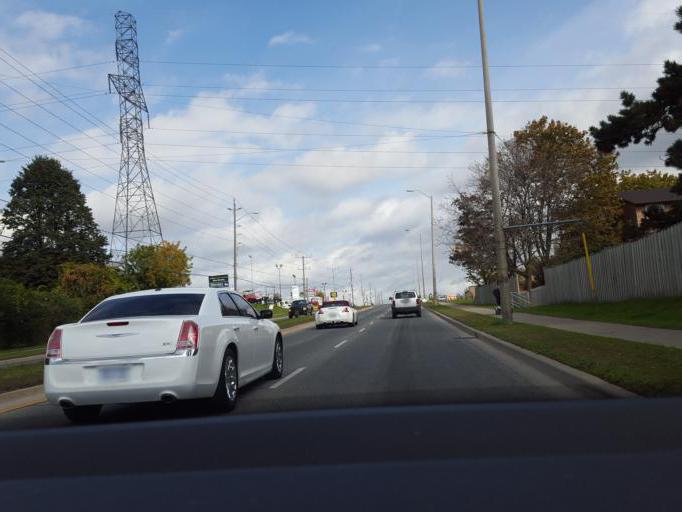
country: CA
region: Ontario
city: Oshawa
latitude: 43.9359
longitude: -78.8655
